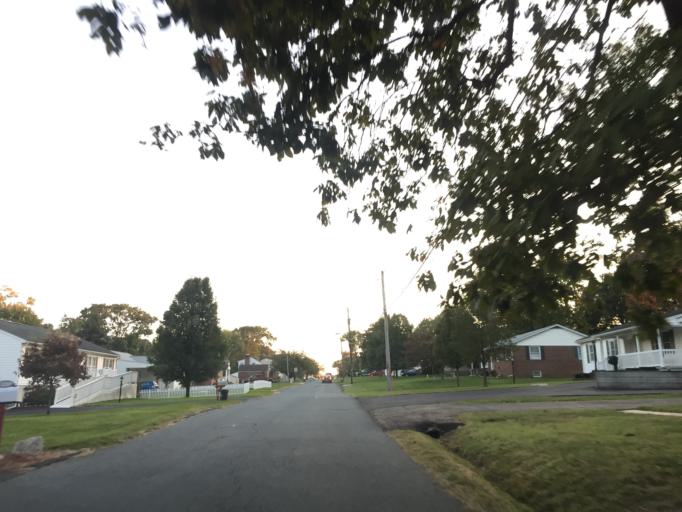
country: US
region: Maryland
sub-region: Baltimore County
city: Essex
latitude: 39.3176
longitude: -76.4723
